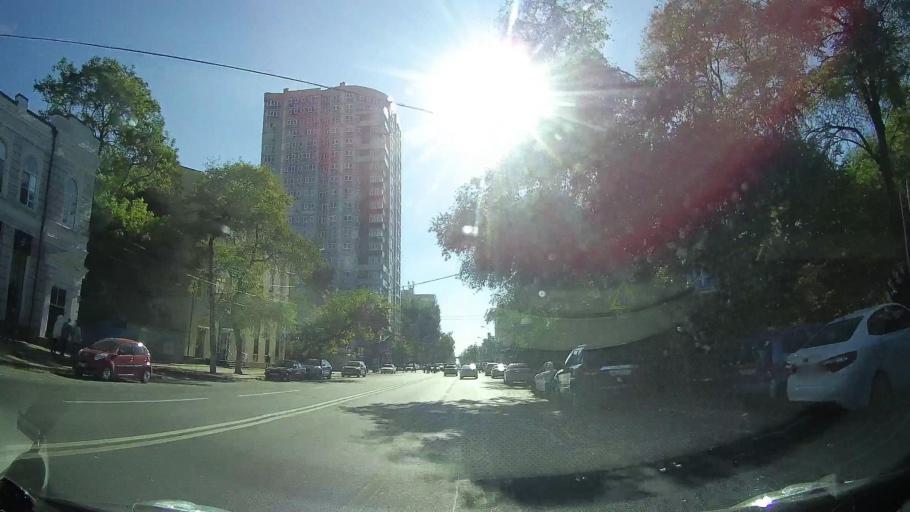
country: RU
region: Rostov
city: Rostov-na-Donu
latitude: 47.2291
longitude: 39.7287
